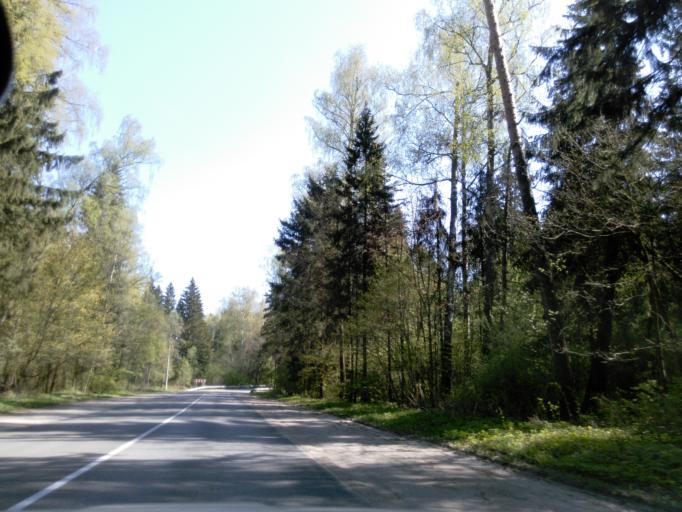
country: RU
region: Moskovskaya
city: Mendeleyevo
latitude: 56.0338
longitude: 37.2238
